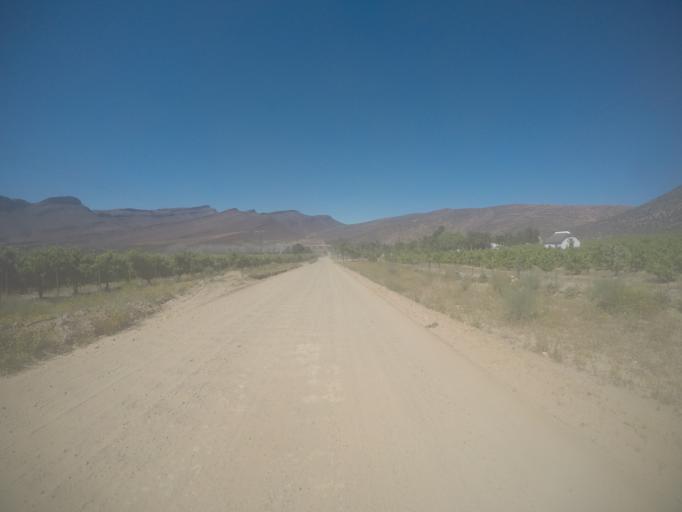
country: ZA
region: Western Cape
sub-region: West Coast District Municipality
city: Clanwilliam
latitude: -32.5604
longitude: 19.3614
